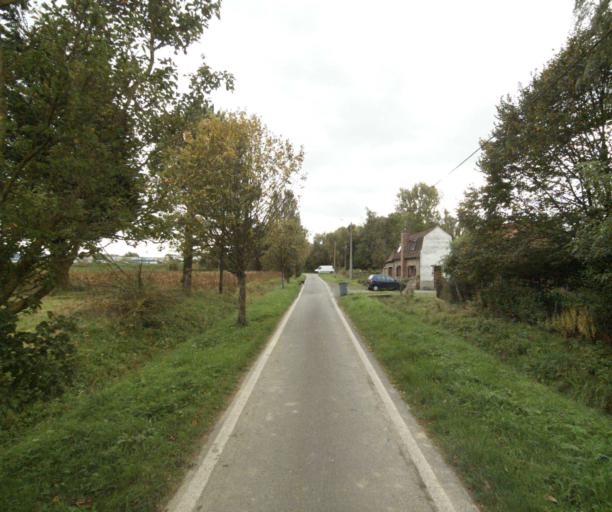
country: FR
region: Nord-Pas-de-Calais
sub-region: Departement du Nord
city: Bois-Grenier
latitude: 50.6574
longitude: 2.9078
